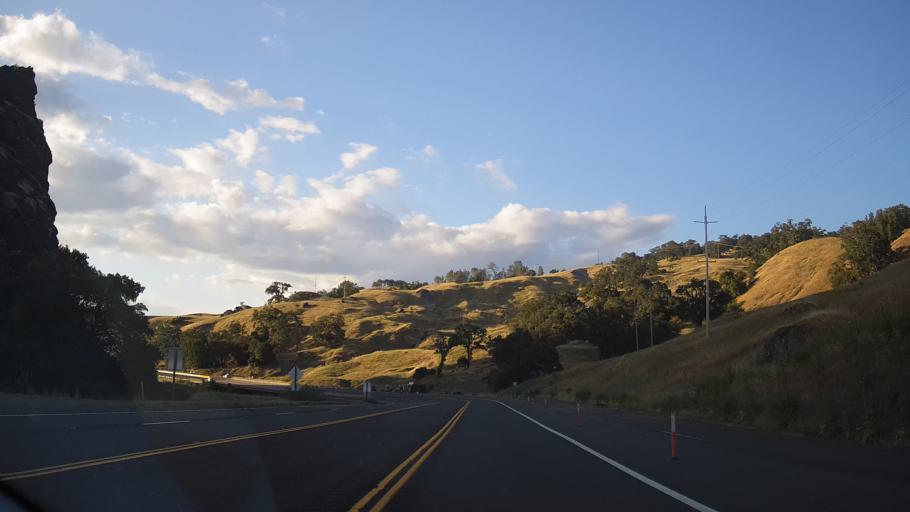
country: US
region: California
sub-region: Sonoma County
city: Cloverdale
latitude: 38.9100
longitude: -123.0541
